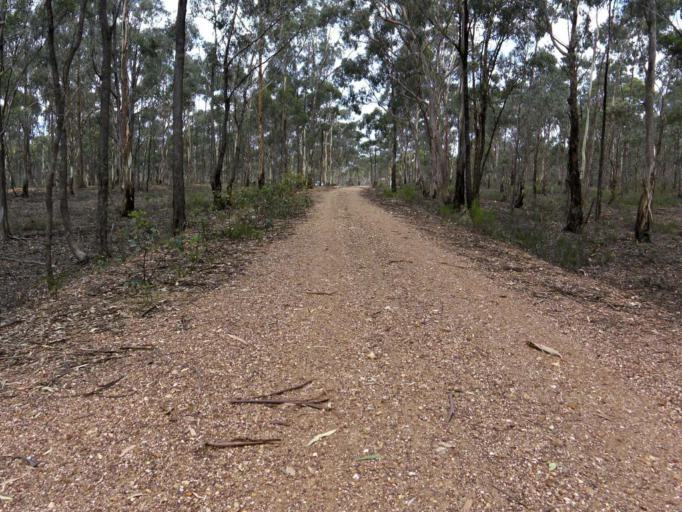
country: AU
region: Victoria
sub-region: Greater Bendigo
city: Kennington
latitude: -36.8901
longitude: 144.6639
